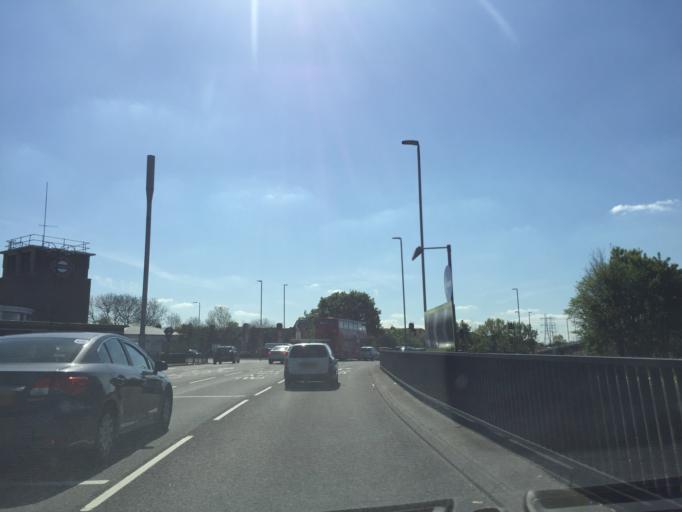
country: GB
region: England
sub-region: Greater London
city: Ilford
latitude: 51.5766
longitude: 0.0446
